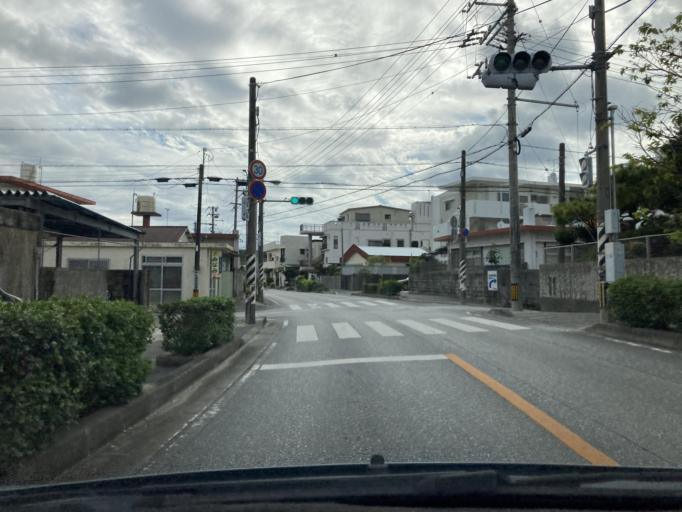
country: JP
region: Okinawa
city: Itoman
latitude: 26.1276
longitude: 127.6776
